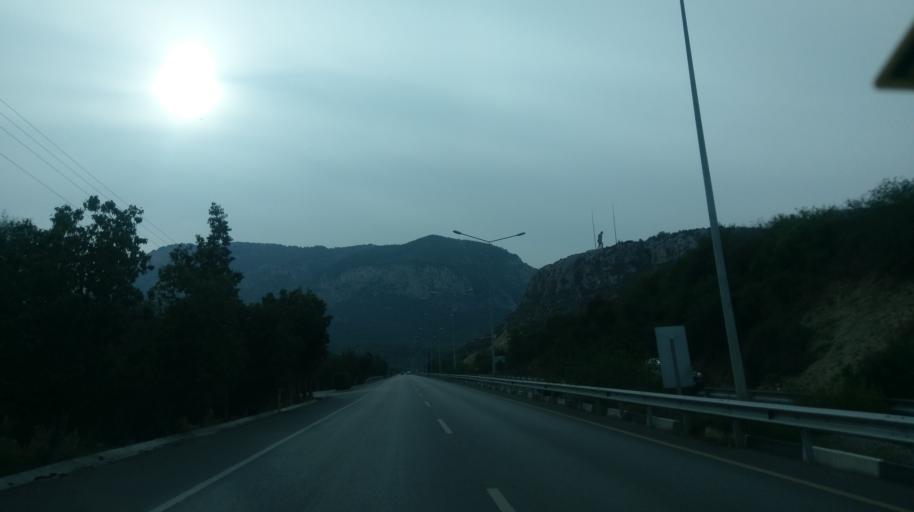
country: CY
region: Keryneia
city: Kyrenia
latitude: 35.3184
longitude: 33.3218
